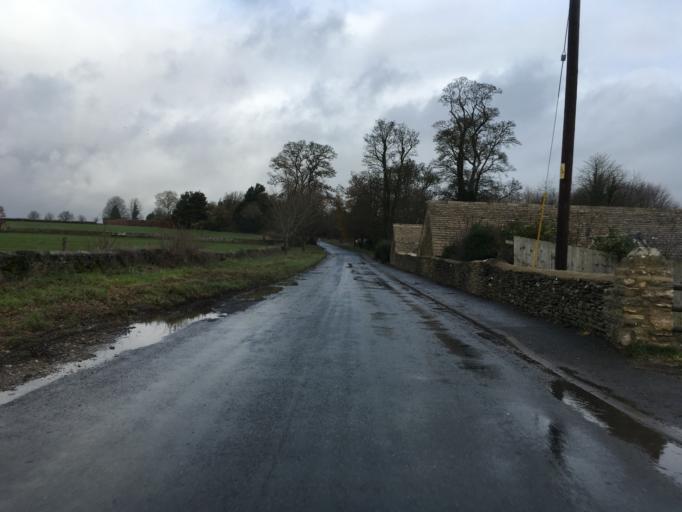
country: GB
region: England
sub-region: Gloucestershire
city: Tetbury
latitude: 51.6271
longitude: -2.1333
